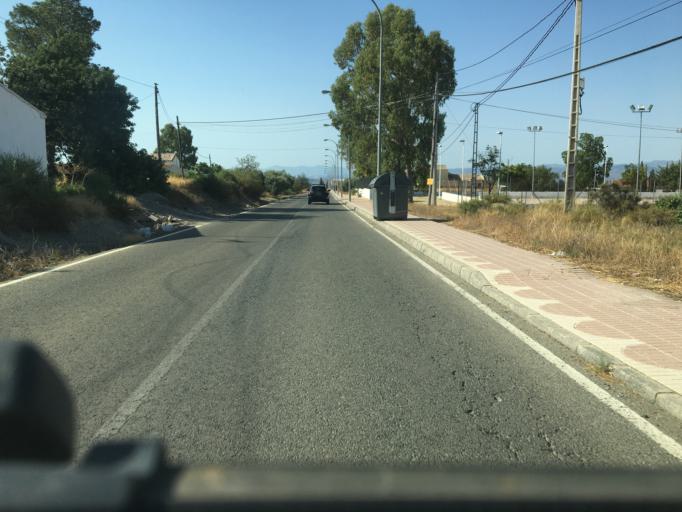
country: ES
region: Andalusia
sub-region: Provincia de Almeria
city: Huercal-Overa
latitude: 37.4587
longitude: -1.9891
